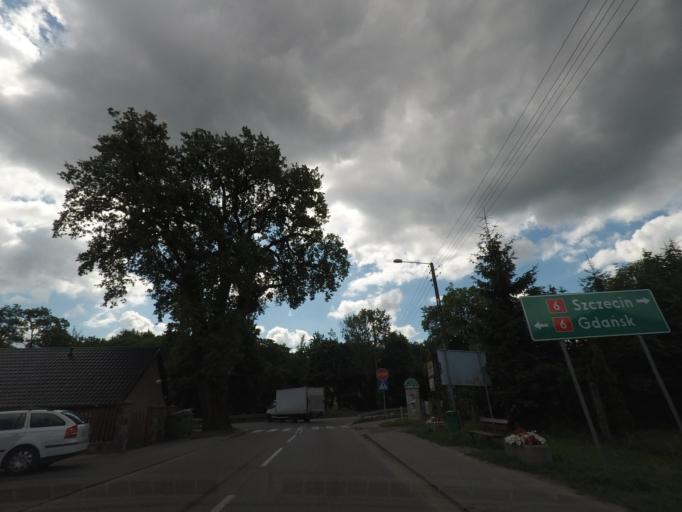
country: PL
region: Pomeranian Voivodeship
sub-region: Powiat wejherowski
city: Leczyce
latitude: 54.5739
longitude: 17.8659
